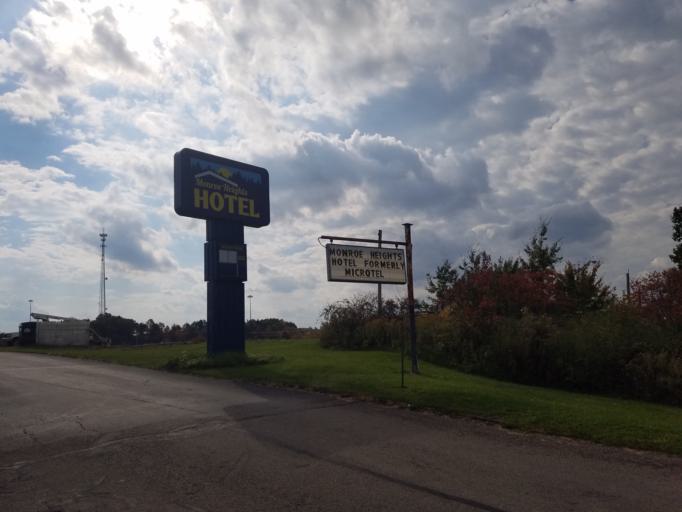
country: US
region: Pennsylvania
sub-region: Clarion County
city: Clarion
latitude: 41.1877
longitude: -79.3915
